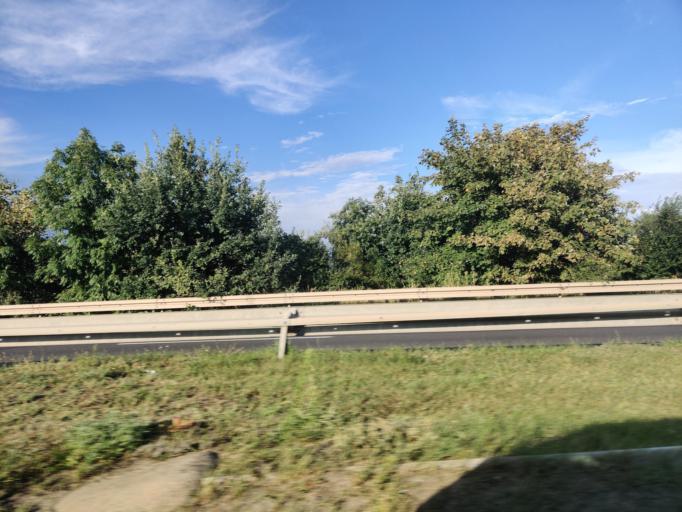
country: PL
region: Greater Poland Voivodeship
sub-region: Konin
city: Konin
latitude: 52.2156
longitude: 18.2557
